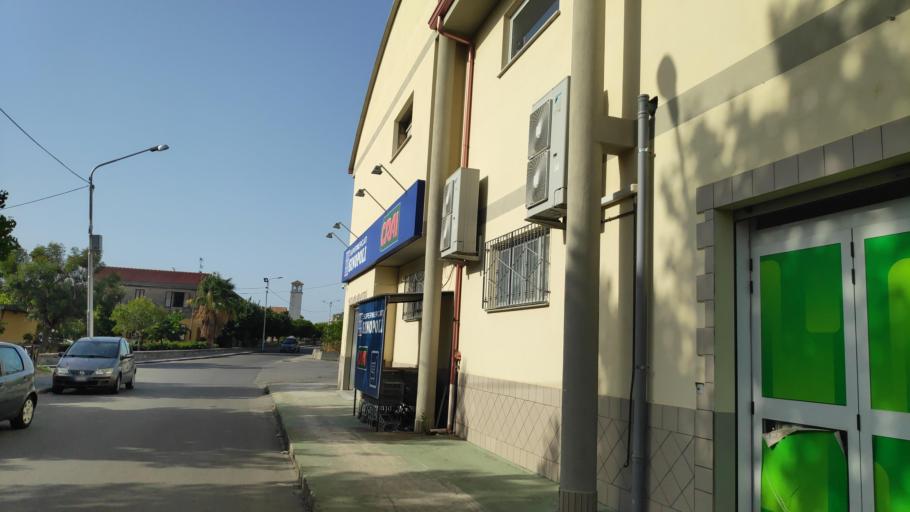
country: IT
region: Calabria
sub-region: Provincia di Catanzaro
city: Santa Caterina dello Ionio Marina
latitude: 38.5317
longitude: 16.5699
